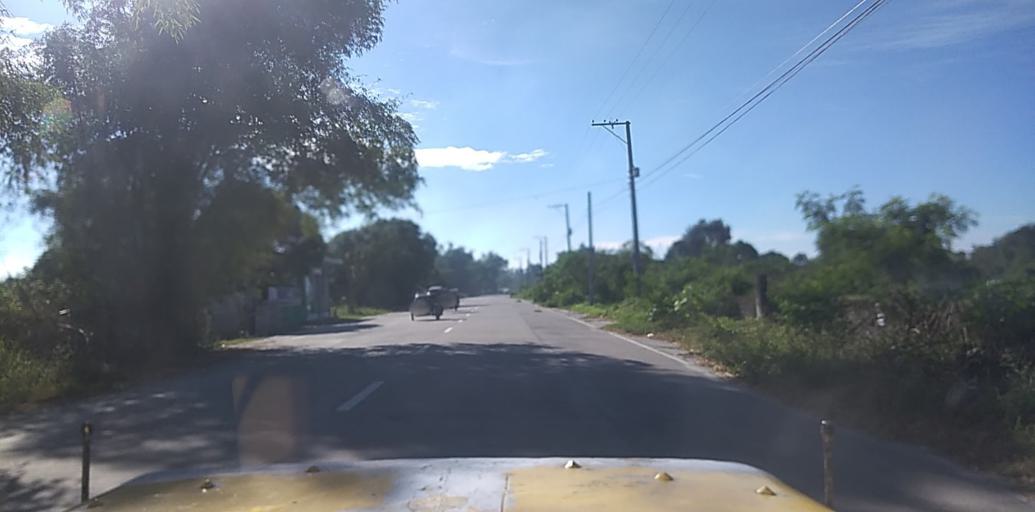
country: PH
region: Central Luzon
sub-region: Province of Pampanga
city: Anao
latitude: 15.1239
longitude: 120.7006
